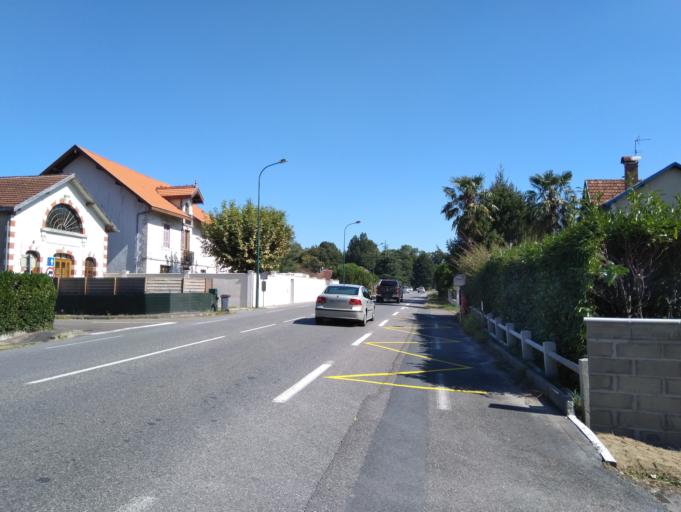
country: FR
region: Aquitaine
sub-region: Departement des Landes
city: Narrosse
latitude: 43.6955
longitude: -1.0166
